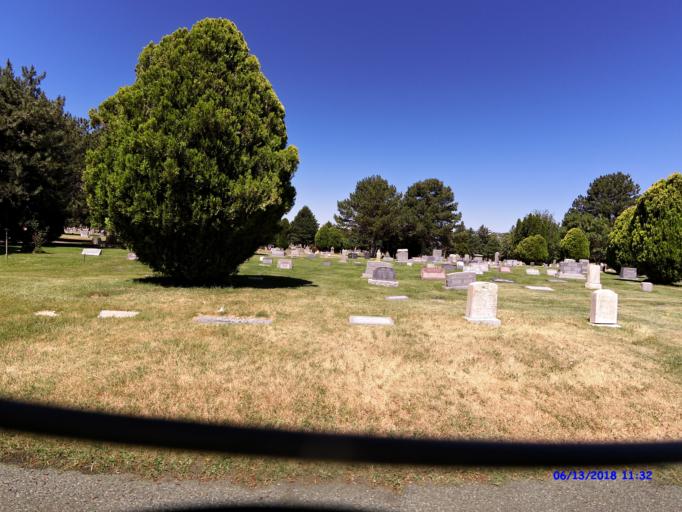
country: US
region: Utah
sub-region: Weber County
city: Ogden
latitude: 41.2328
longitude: -111.9628
